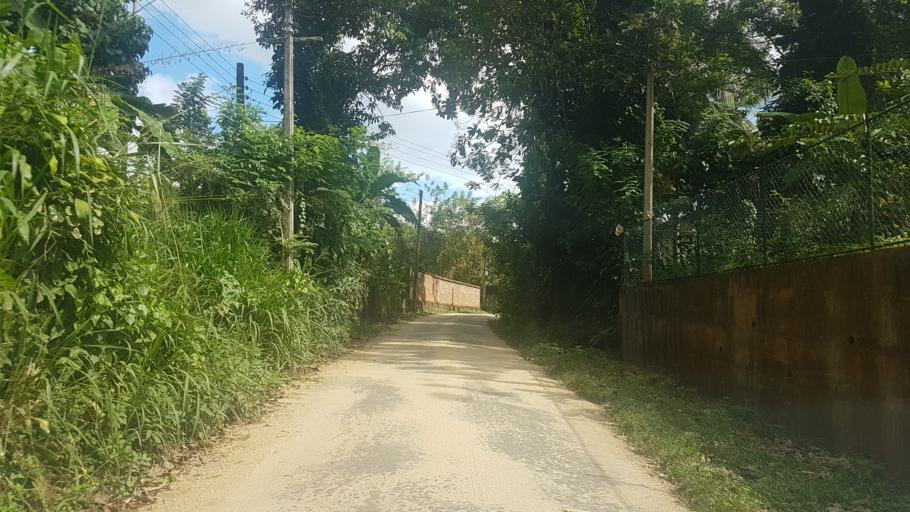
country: LK
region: Central
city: Gampola
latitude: 7.2198
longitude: 80.5862
